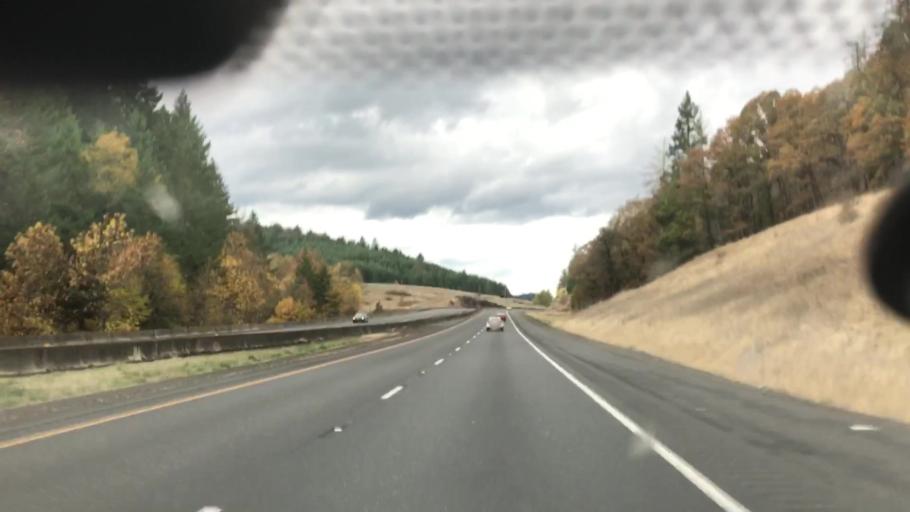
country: US
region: Oregon
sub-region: Douglas County
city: Sutherlin
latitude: 43.4865
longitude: -123.3270
